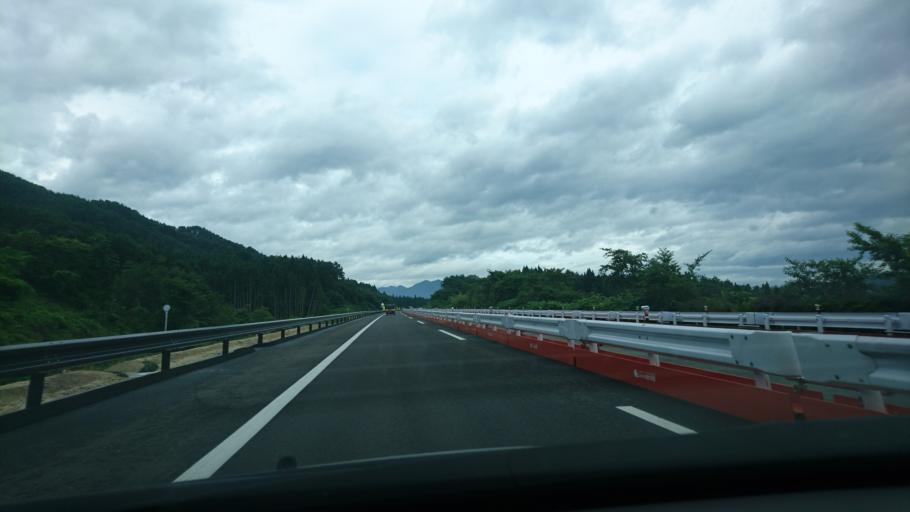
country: JP
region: Iwate
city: Yamada
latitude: 39.4250
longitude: 141.9691
